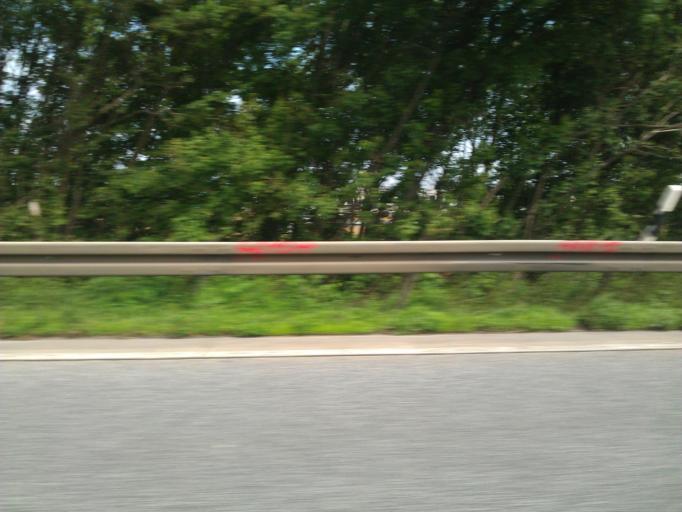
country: DE
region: North Rhine-Westphalia
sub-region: Regierungsbezirk Koln
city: Wurselen
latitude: 50.8032
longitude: 6.1515
